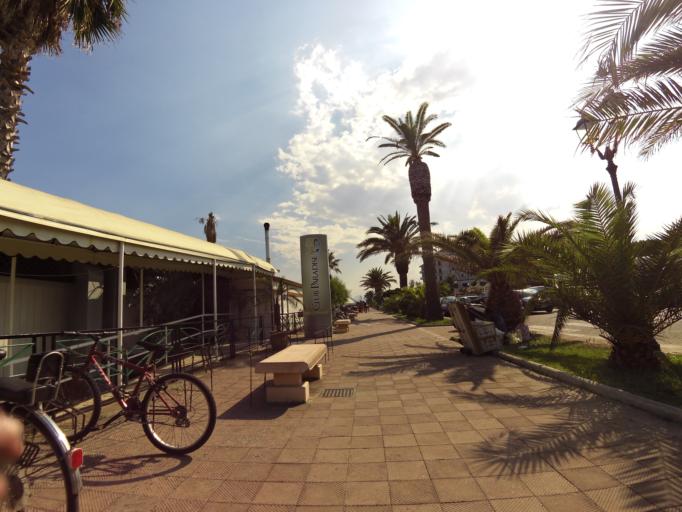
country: IT
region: Calabria
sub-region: Provincia di Reggio Calabria
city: Siderno
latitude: 38.2663
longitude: 16.2975
